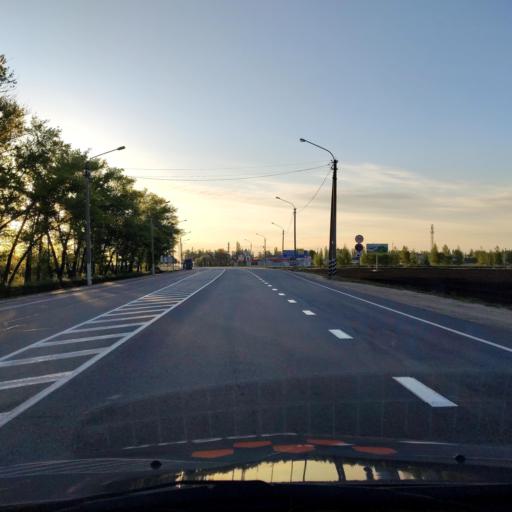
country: RU
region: Orjol
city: Livny
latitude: 52.4411
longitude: 37.5728
